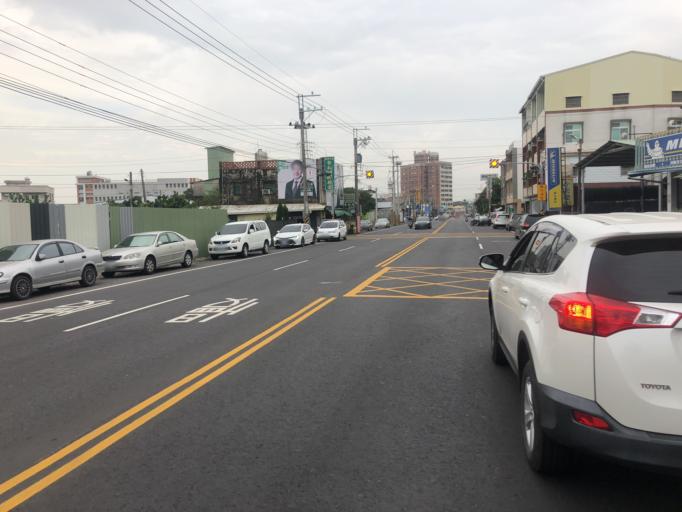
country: TW
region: Taiwan
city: Xinying
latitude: 23.1740
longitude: 120.2465
